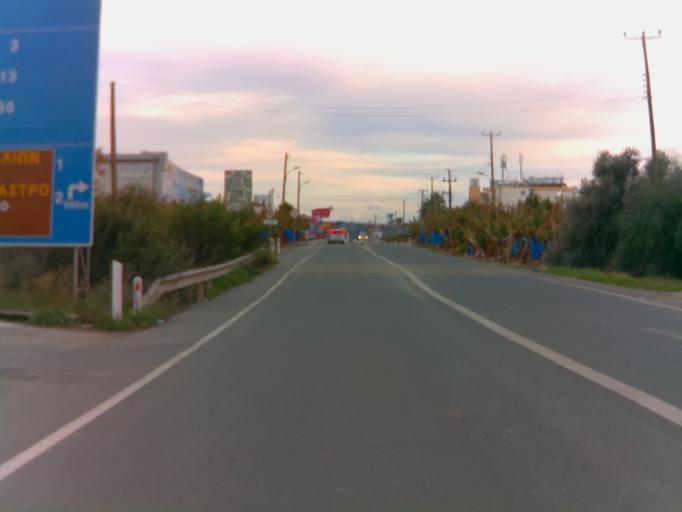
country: CY
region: Pafos
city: Pegeia
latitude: 34.8584
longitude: 32.3758
